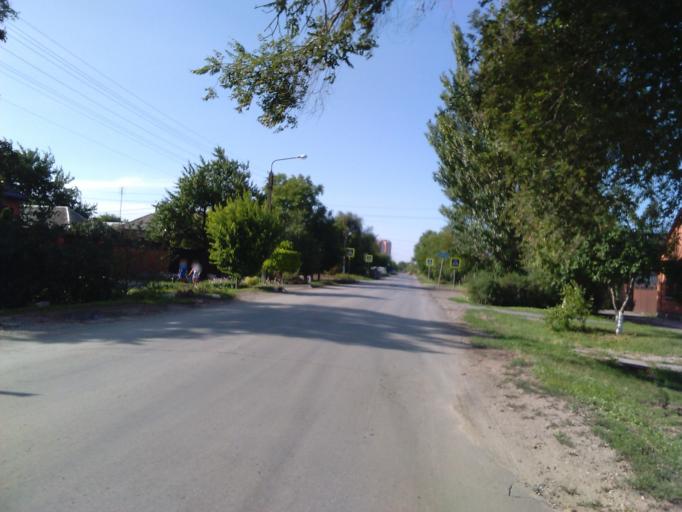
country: RU
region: Rostov
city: Bataysk
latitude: 47.1443
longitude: 39.7355
